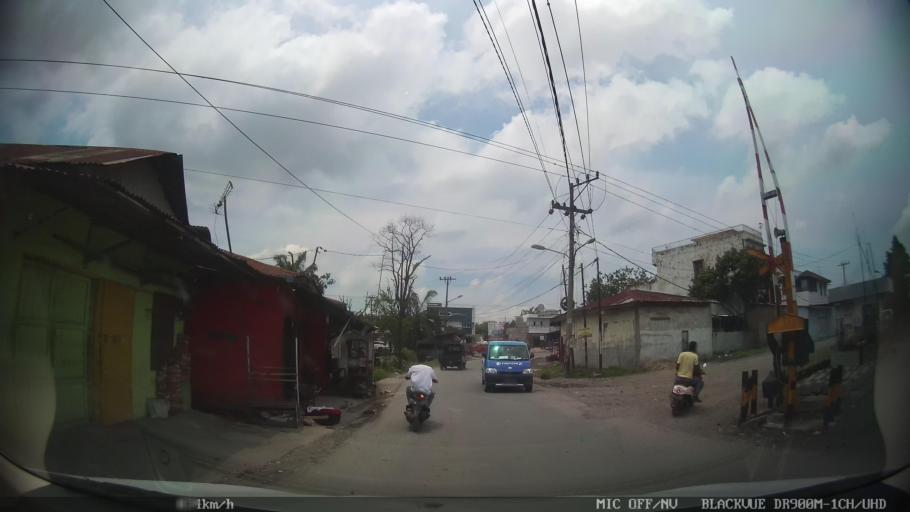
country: ID
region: North Sumatra
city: Labuhan Deli
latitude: 3.6846
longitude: 98.6674
